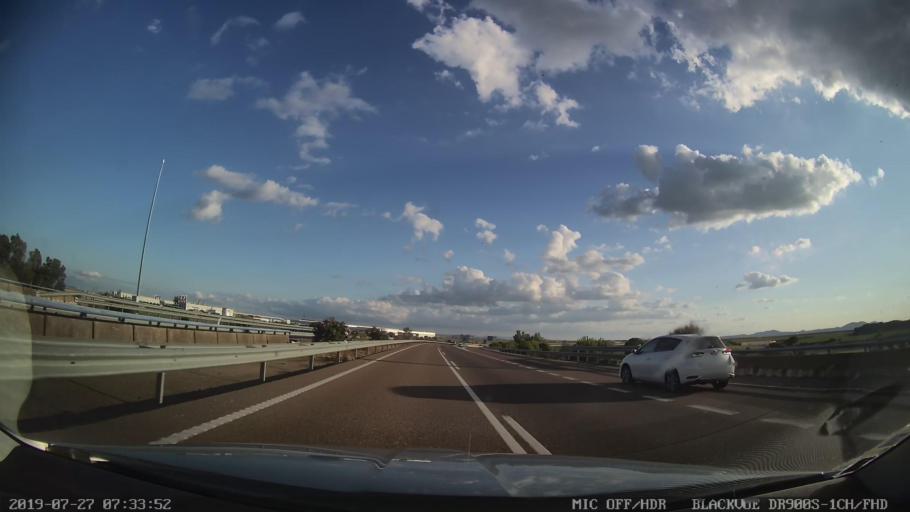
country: ES
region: Extremadura
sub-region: Provincia de Caceres
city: Miajadas
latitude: 39.1357
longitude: -5.9451
